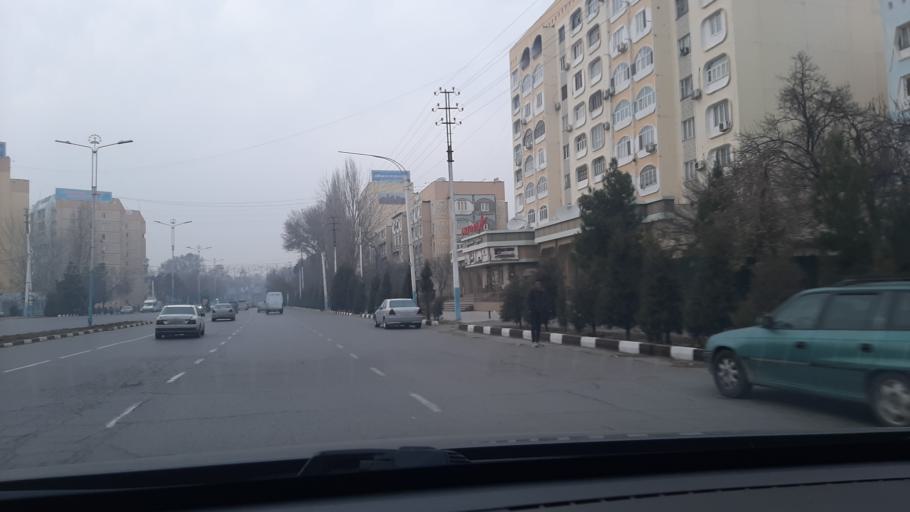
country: TJ
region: Viloyati Sughd
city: Khujand
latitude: 40.2667
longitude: 69.6525
